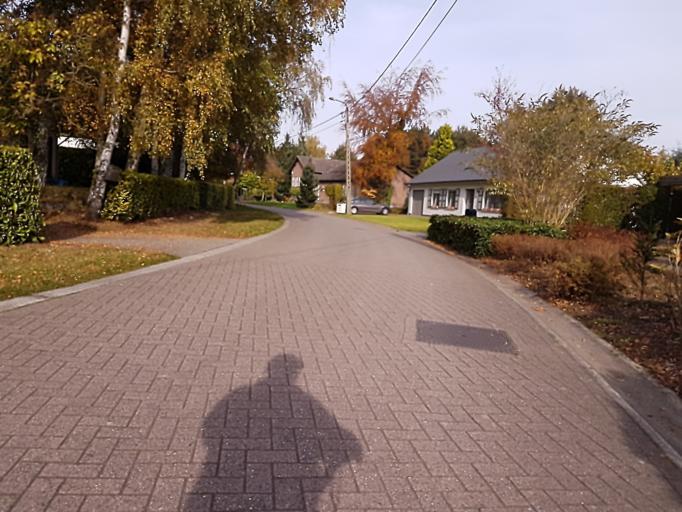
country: BE
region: Flanders
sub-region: Provincie Antwerpen
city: Sint-Katelijne-Waver
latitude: 51.0594
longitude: 4.5177
